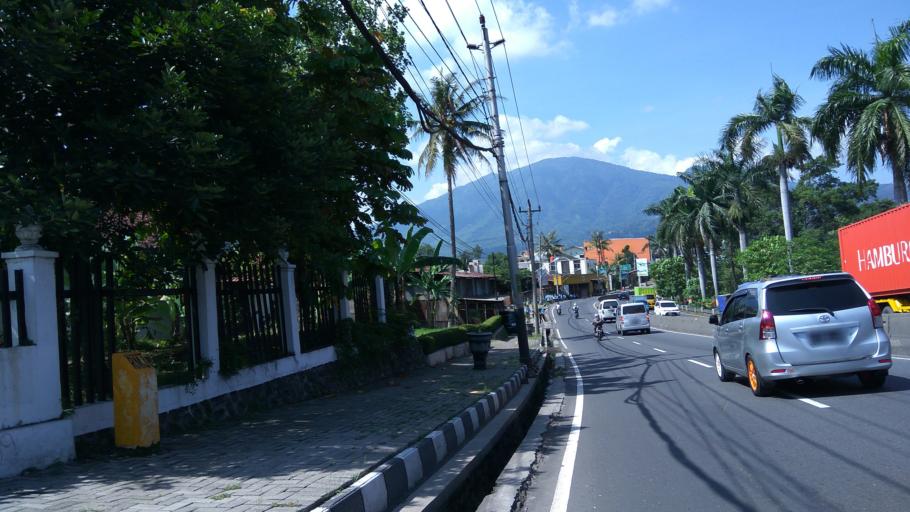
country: ID
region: Central Java
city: Ungaran
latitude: -7.1201
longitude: 110.4107
